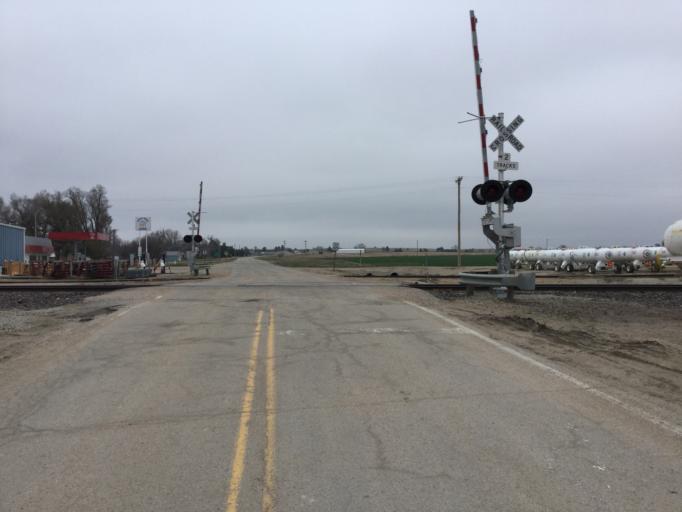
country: US
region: Kansas
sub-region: Russell County
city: Russell
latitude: 38.8462
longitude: -98.5854
